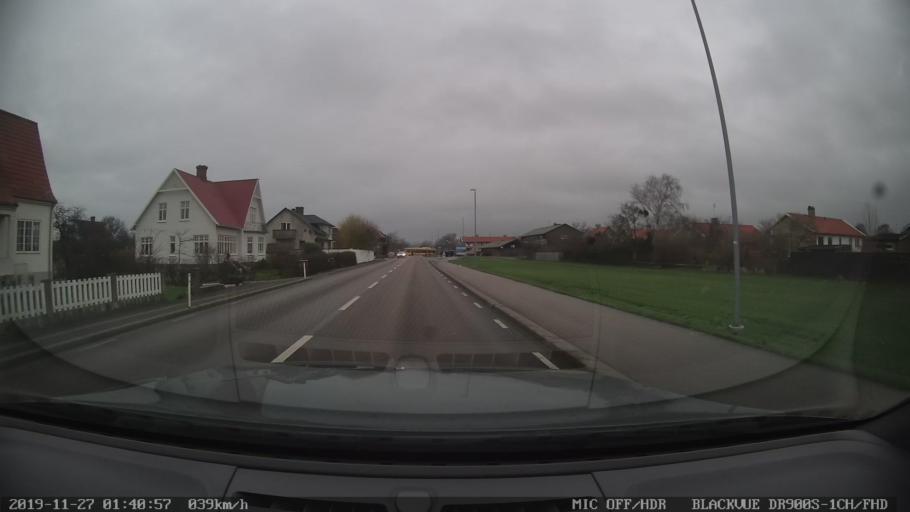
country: SE
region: Skane
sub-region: Hoganas Kommun
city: Hoganas
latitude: 56.2411
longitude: 12.5404
